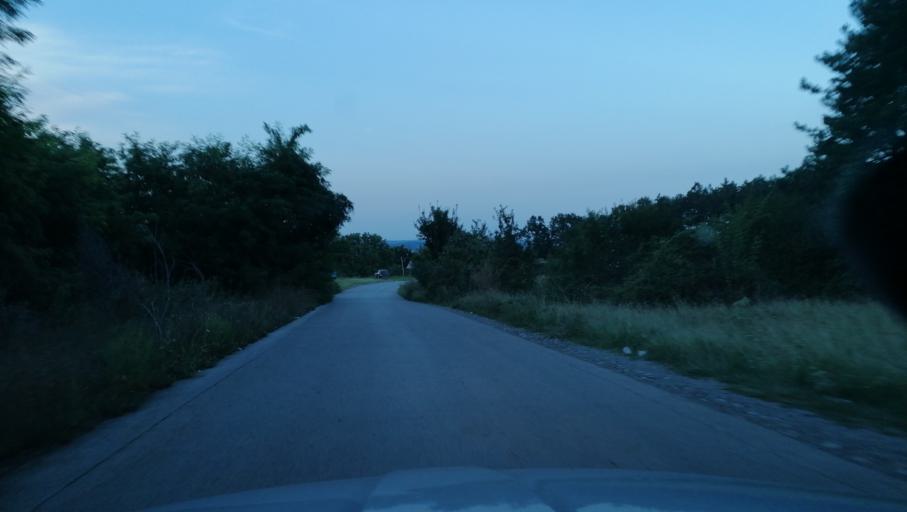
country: RS
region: Central Serbia
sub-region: Kolubarski Okrug
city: Valjevo
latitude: 44.2515
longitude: 19.8756
